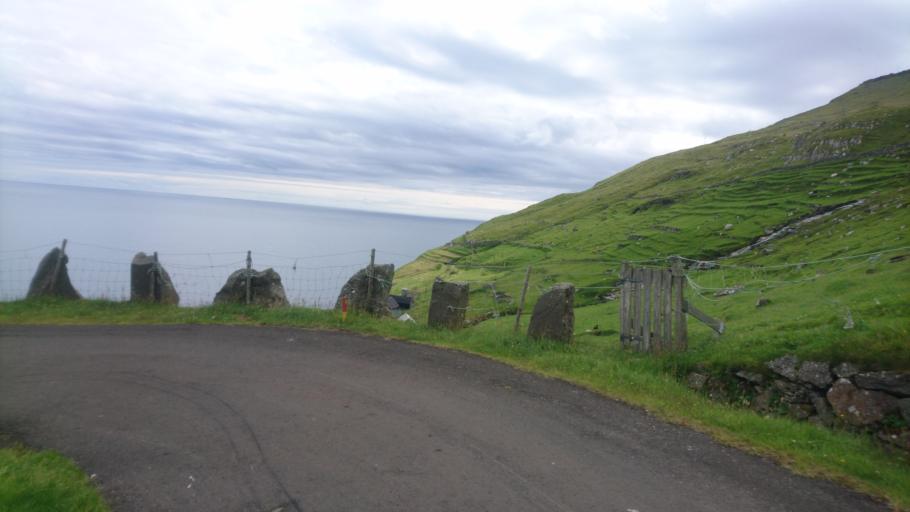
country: FO
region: Nordoyar
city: Klaksvik
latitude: 62.3300
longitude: -6.2782
